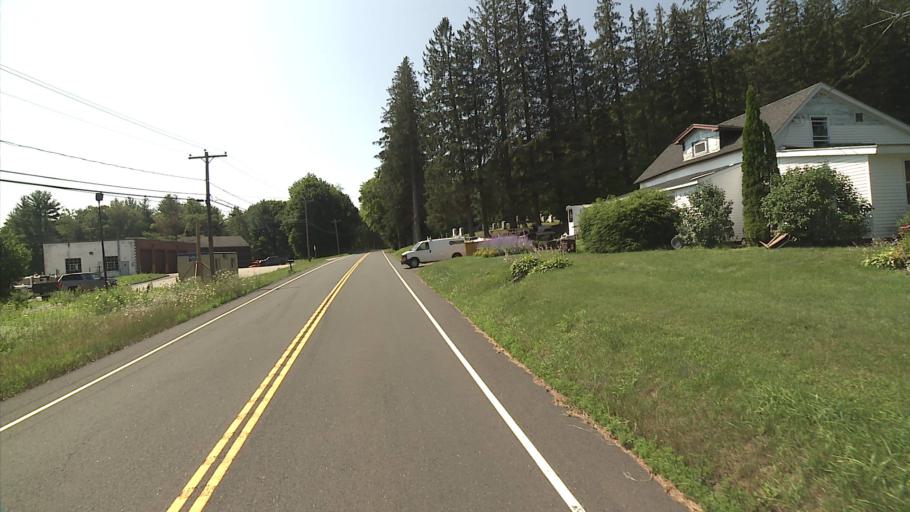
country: US
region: Massachusetts
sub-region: Berkshire County
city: New Marlborough
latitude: 42.0076
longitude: -73.2037
